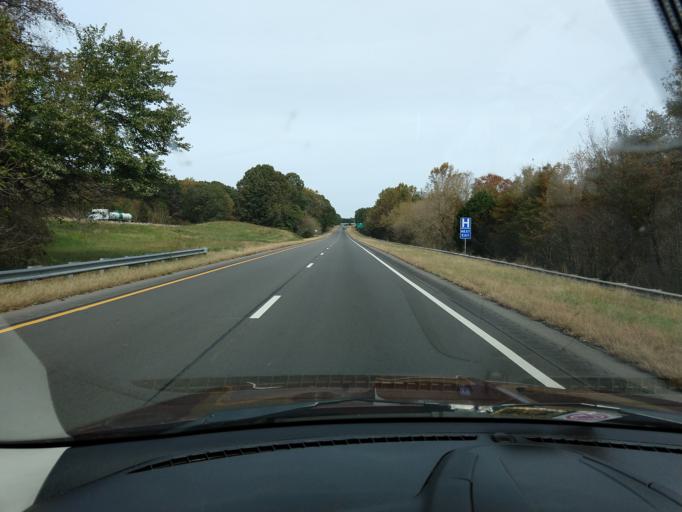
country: US
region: Virginia
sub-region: Pittsylvania County
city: Gretna
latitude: 36.9453
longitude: -79.3775
